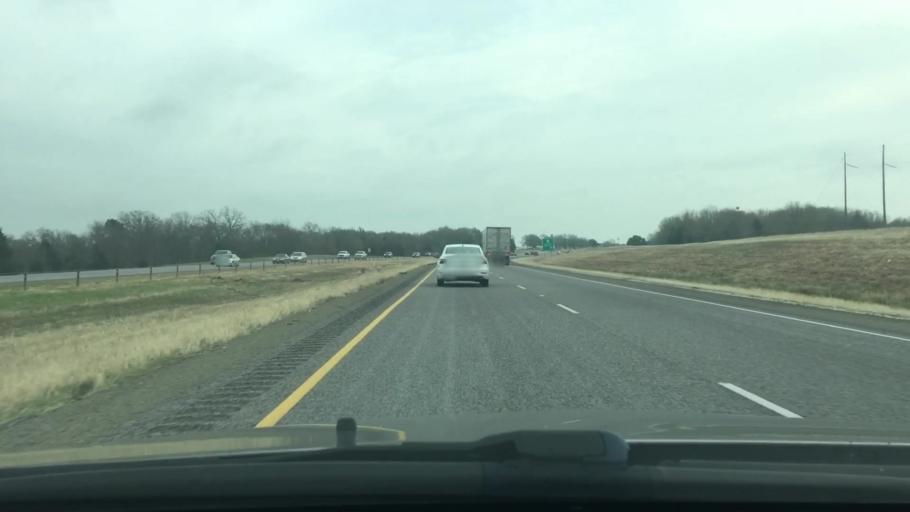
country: US
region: Texas
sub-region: Freestone County
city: Fairfield
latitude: 31.7345
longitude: -96.1848
